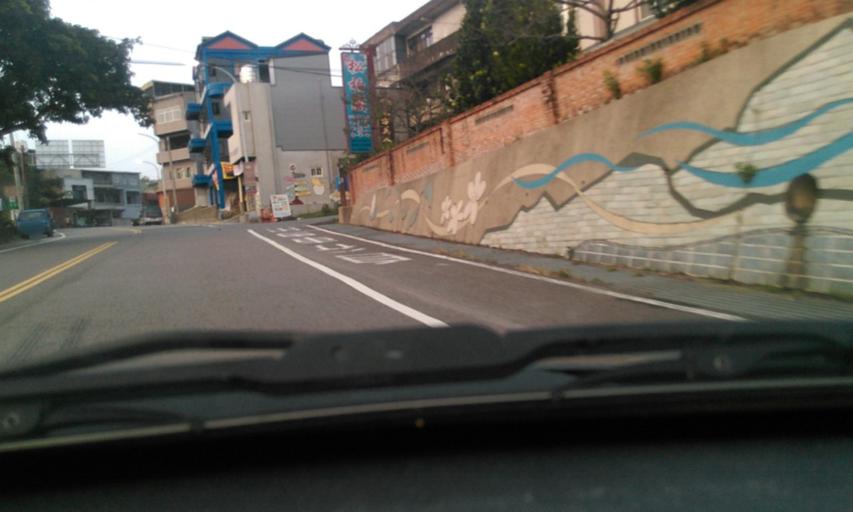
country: TW
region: Taiwan
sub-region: Hsinchu
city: Hsinchu
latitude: 24.6869
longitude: 120.9873
